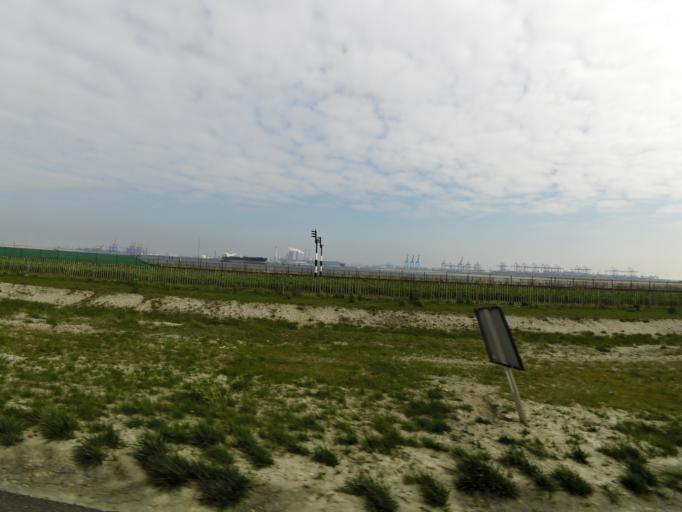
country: NL
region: South Holland
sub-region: Gemeente Rotterdam
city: Hoek van Holland
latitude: 51.9754
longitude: 3.9758
